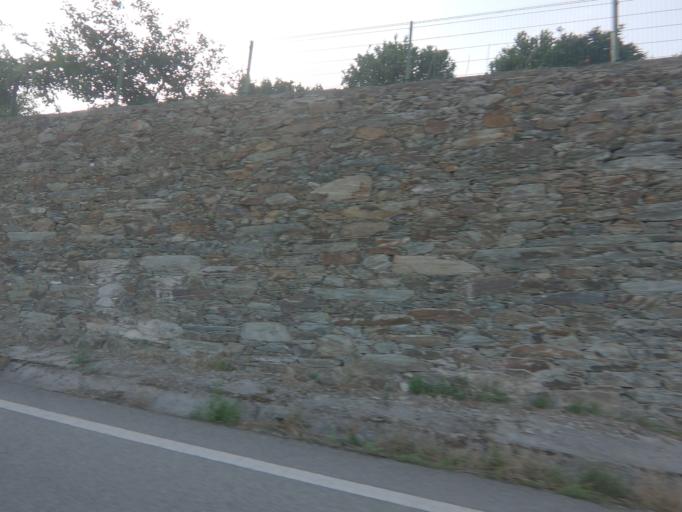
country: PT
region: Vila Real
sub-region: Sabrosa
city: Vilela
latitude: 41.1961
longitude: -7.5424
